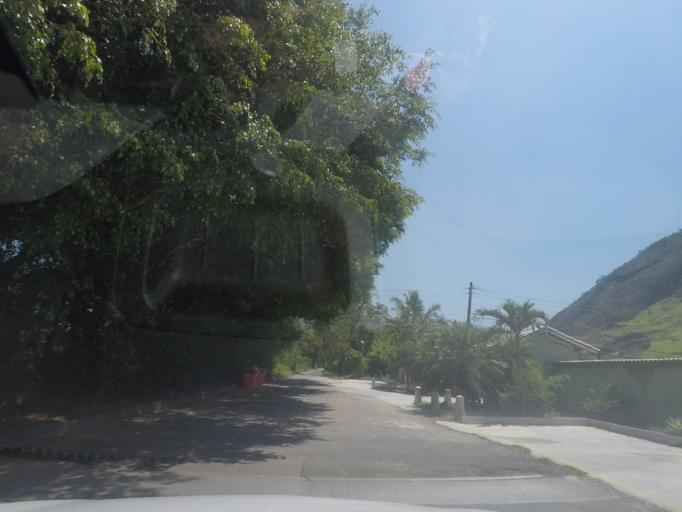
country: BR
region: Rio de Janeiro
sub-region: Nilopolis
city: Nilopolis
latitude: -22.9912
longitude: -43.4560
